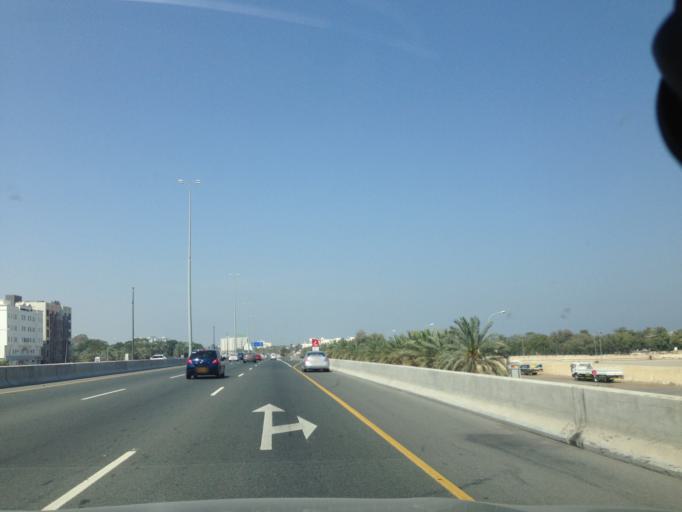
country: OM
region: Muhafazat Masqat
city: As Sib al Jadidah
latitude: 23.6427
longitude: 58.2229
